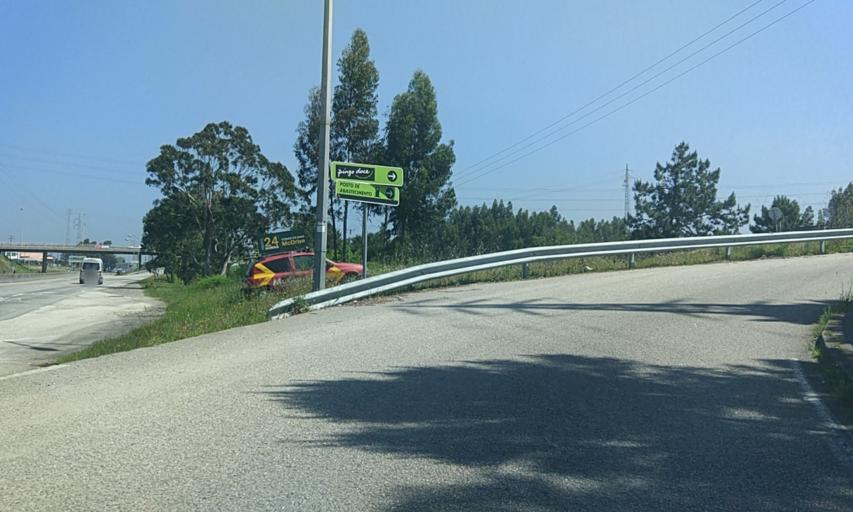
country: PT
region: Aveiro
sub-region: Aveiro
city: Aveiro
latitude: 40.6524
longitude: -8.6209
